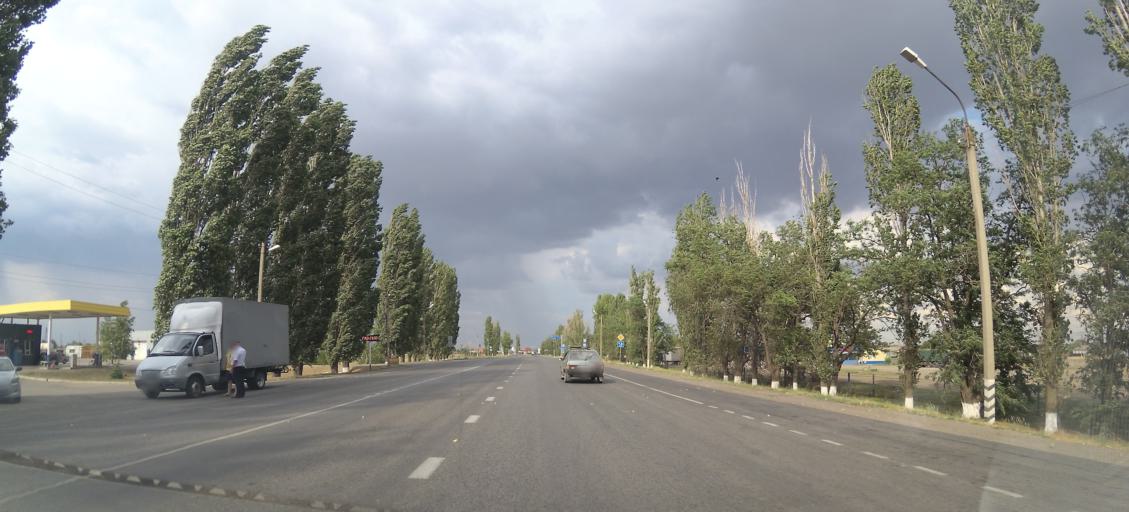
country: RU
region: Rostov
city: Zimovniki
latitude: 47.1416
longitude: 42.4369
